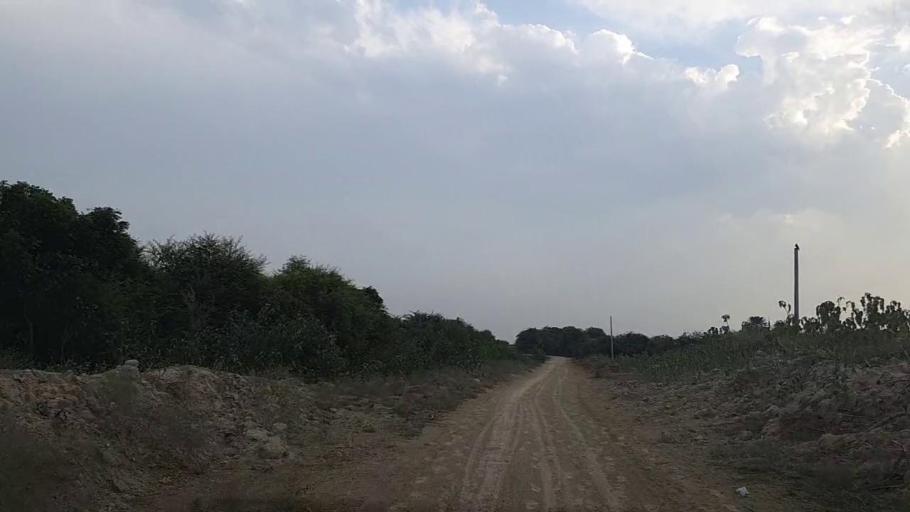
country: PK
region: Sindh
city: Daro Mehar
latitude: 24.7662
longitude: 68.1539
